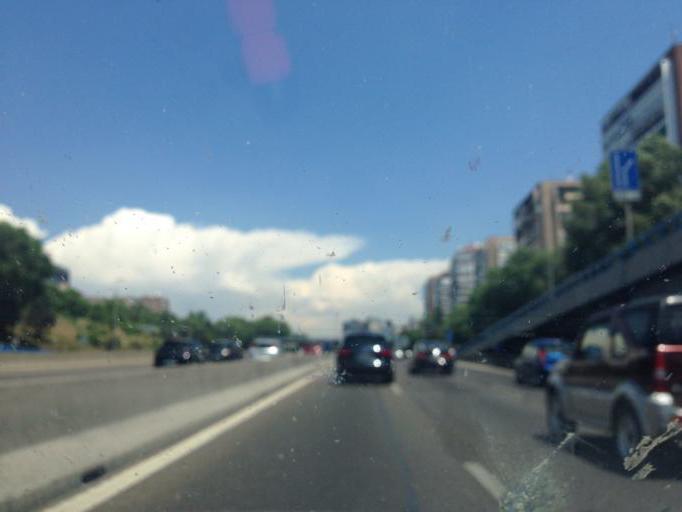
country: ES
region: Madrid
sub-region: Provincia de Madrid
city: Moratalaz
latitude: 40.4322
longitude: -3.6605
